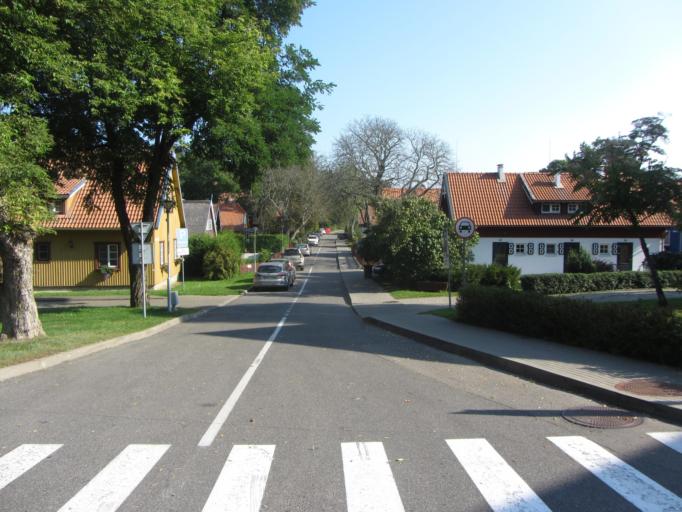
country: LT
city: Nida
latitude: 55.3112
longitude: 21.0102
